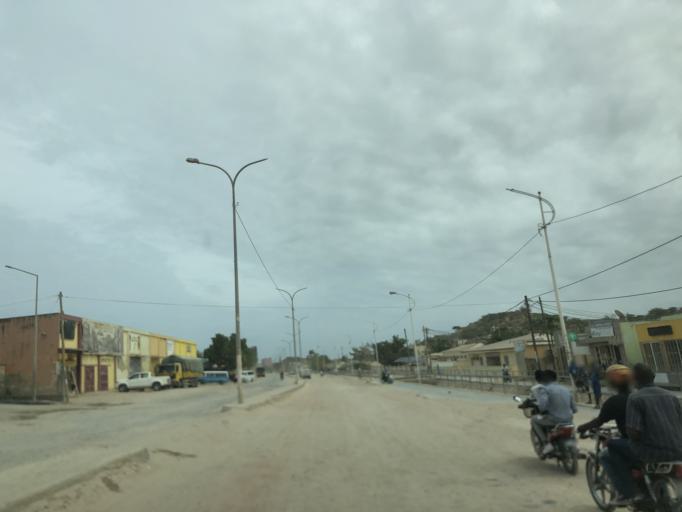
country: AO
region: Cuanza Sul
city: Sumbe
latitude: -11.2122
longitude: 13.8465
